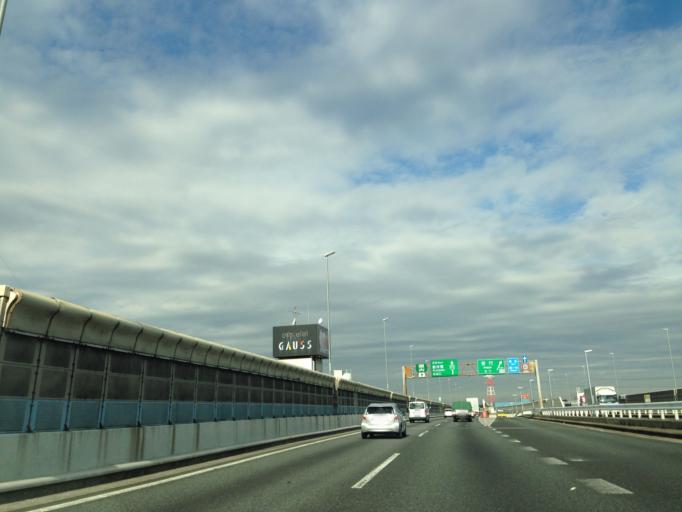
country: JP
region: Saitama
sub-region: Kawaguchi-shi
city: Hatogaya-honcho
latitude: 35.8322
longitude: 139.7566
